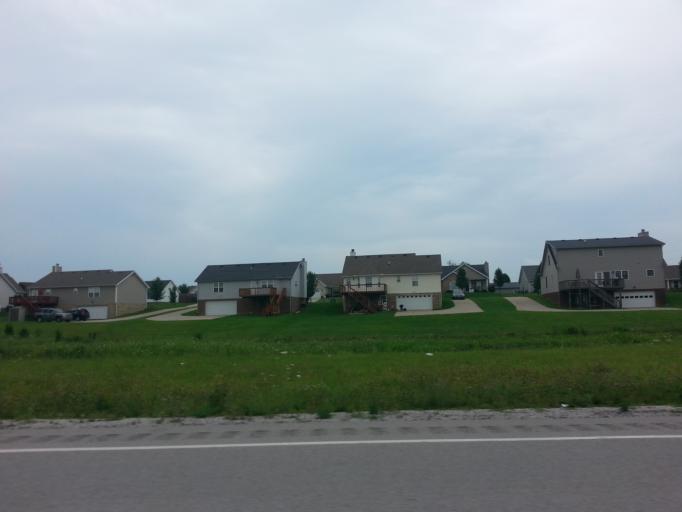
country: US
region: Ohio
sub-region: Brown County
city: Aberdeen
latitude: 38.6066
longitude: -83.8293
